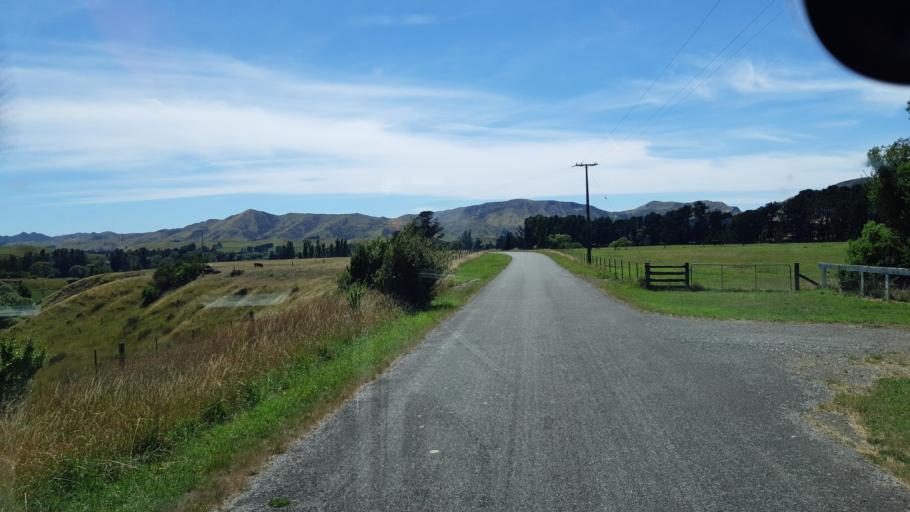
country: NZ
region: Marlborough
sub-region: Marlborough District
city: Blenheim
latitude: -41.8289
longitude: 174.1135
